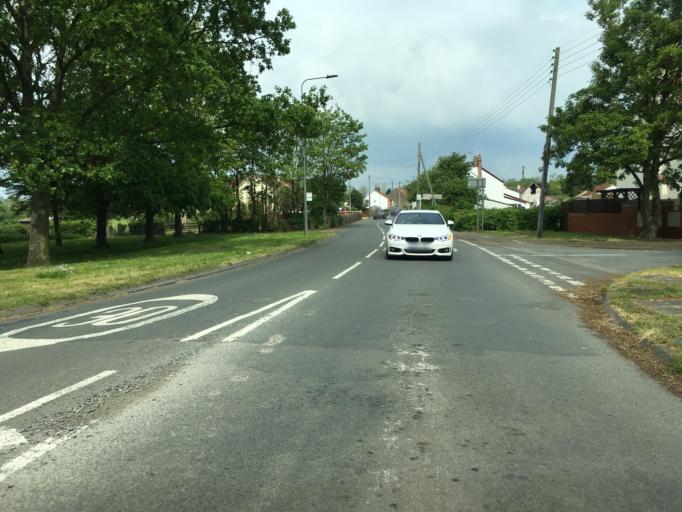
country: GB
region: England
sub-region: South Gloucestershire
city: Severn Beach
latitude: 51.5652
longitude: -2.6478
